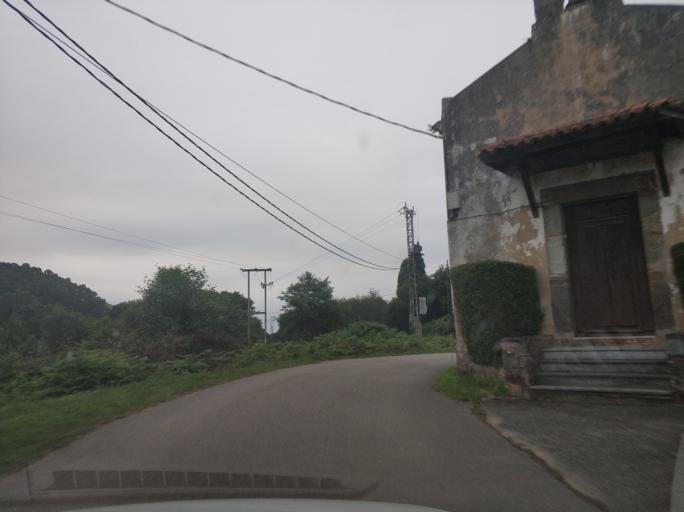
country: ES
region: Asturias
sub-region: Province of Asturias
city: Cudillero
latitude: 43.5589
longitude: -6.1882
